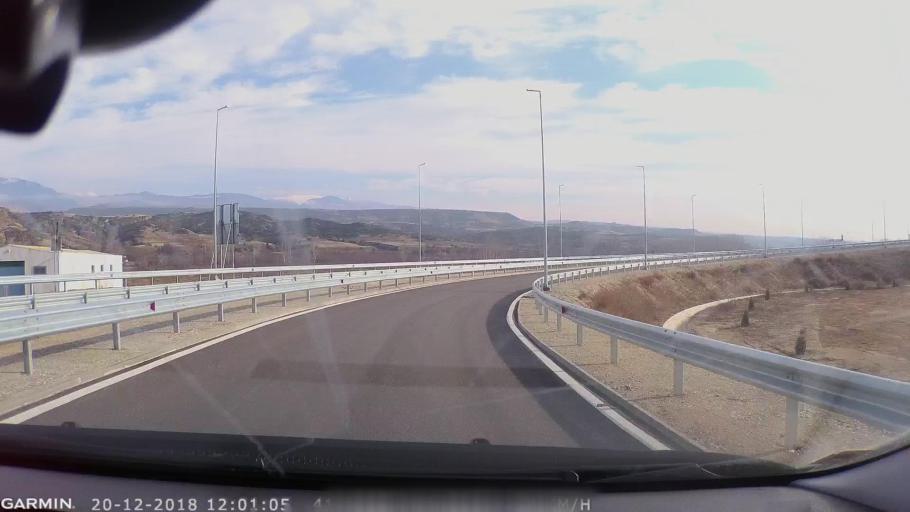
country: BG
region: Blagoevgrad
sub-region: Obshtina Strumyani
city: Strumyani
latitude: 41.6289
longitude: 23.2044
